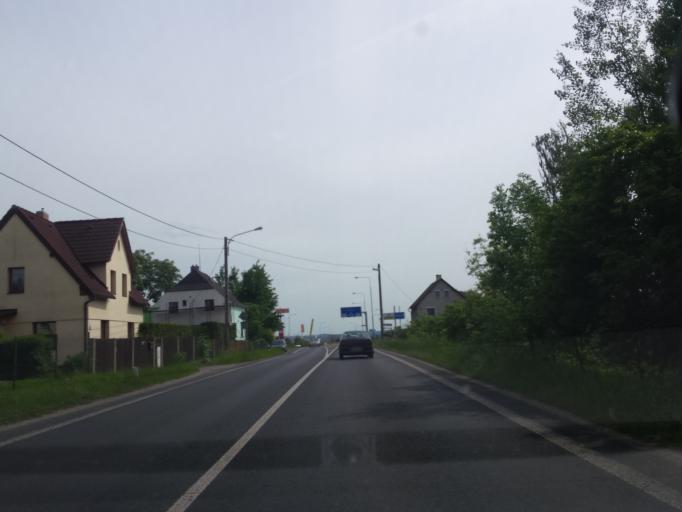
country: CZ
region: Liberecky
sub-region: Okres Ceska Lipa
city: Ceska Lipa
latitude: 50.7027
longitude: 14.5429
